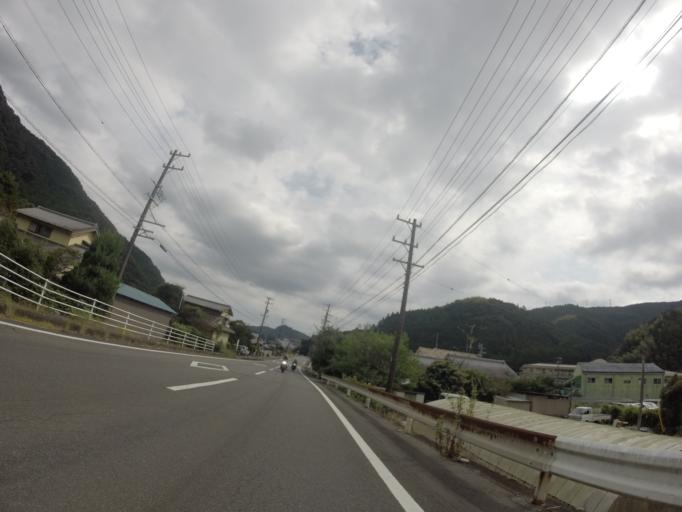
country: JP
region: Shizuoka
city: Fujieda
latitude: 34.9010
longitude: 138.1999
